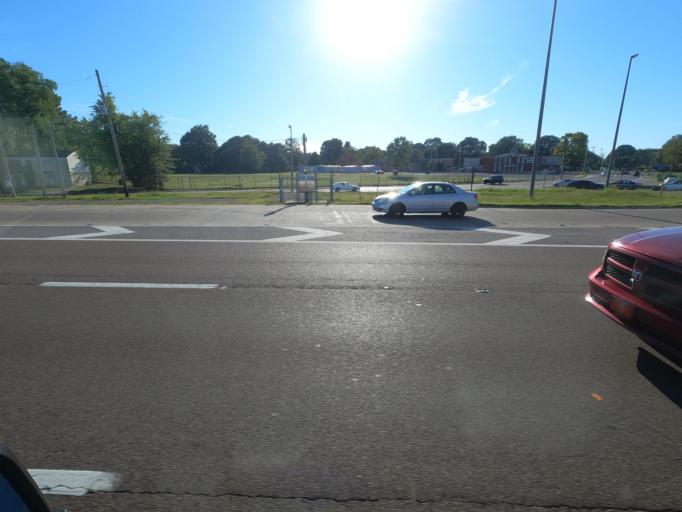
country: US
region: Tennessee
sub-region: Shelby County
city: Bartlett
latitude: 35.1585
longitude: -89.8946
